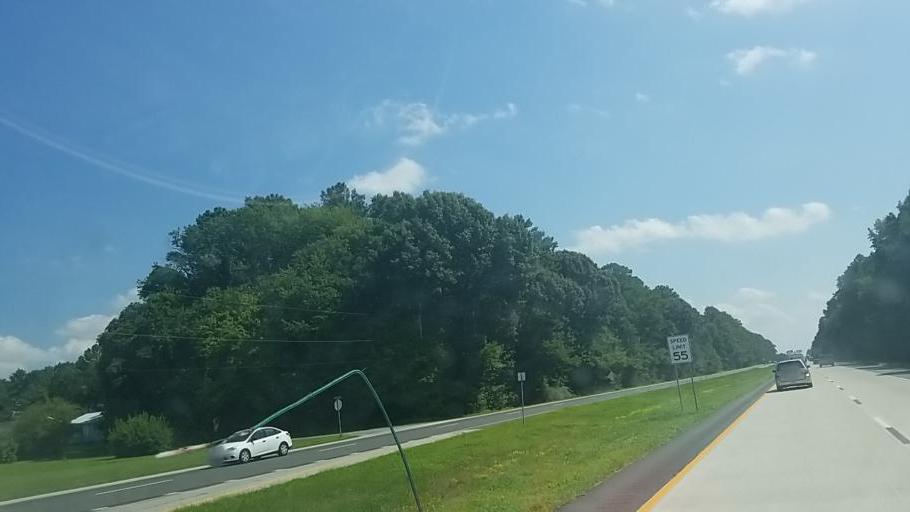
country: US
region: Delaware
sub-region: Sussex County
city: Milford
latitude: 38.8678
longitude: -75.4395
